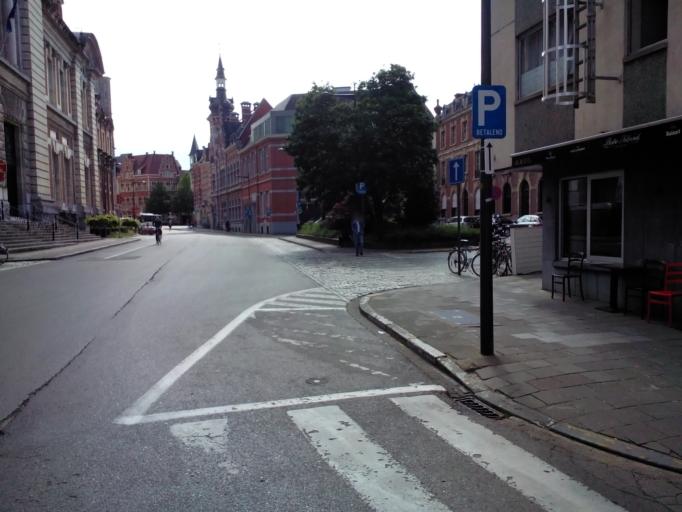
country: BE
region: Flanders
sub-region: Provincie Vlaams-Brabant
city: Leuven
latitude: 50.8808
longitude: 4.7022
